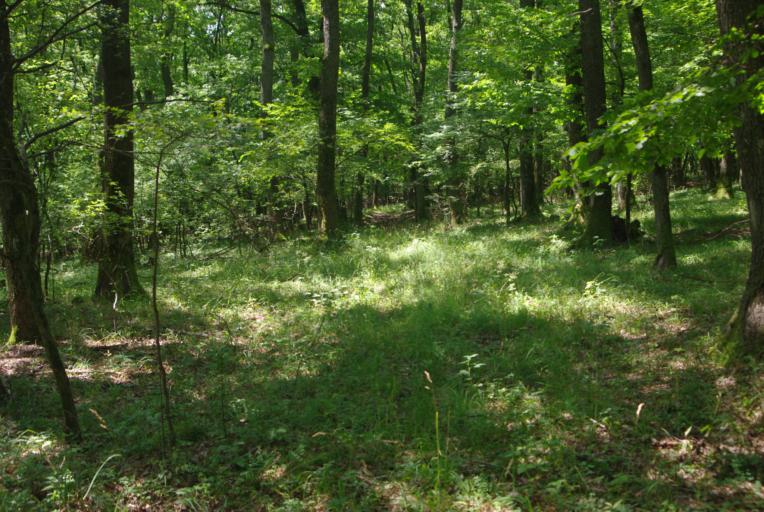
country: HU
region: Borsod-Abauj-Zemplen
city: Gonc
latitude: 48.4071
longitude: 21.3043
